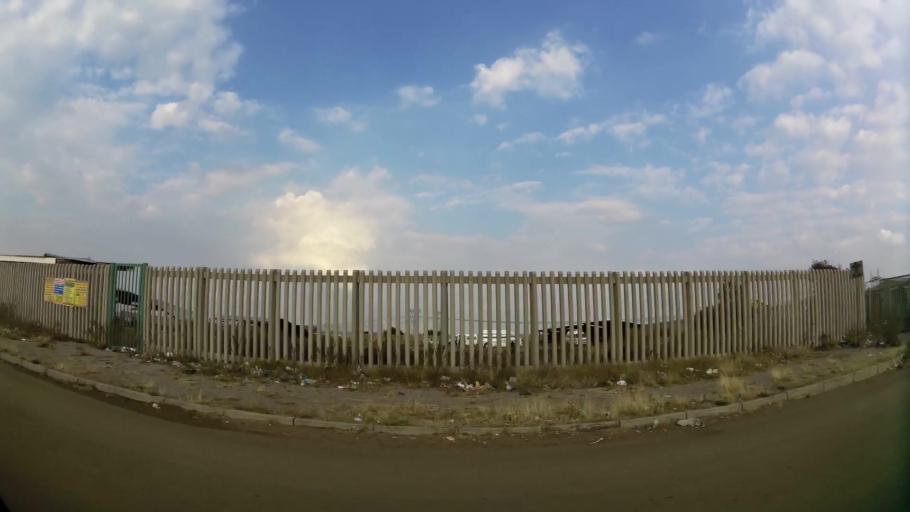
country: ZA
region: Gauteng
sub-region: Sedibeng District Municipality
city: Vanderbijlpark
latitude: -26.6944
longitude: 27.8781
